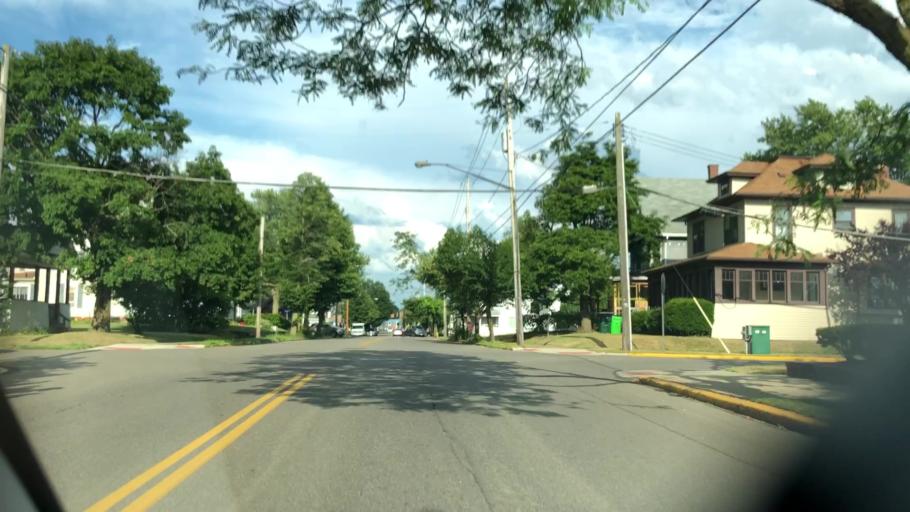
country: US
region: Ohio
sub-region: Summit County
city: Barberton
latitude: 41.0177
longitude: -81.6126
